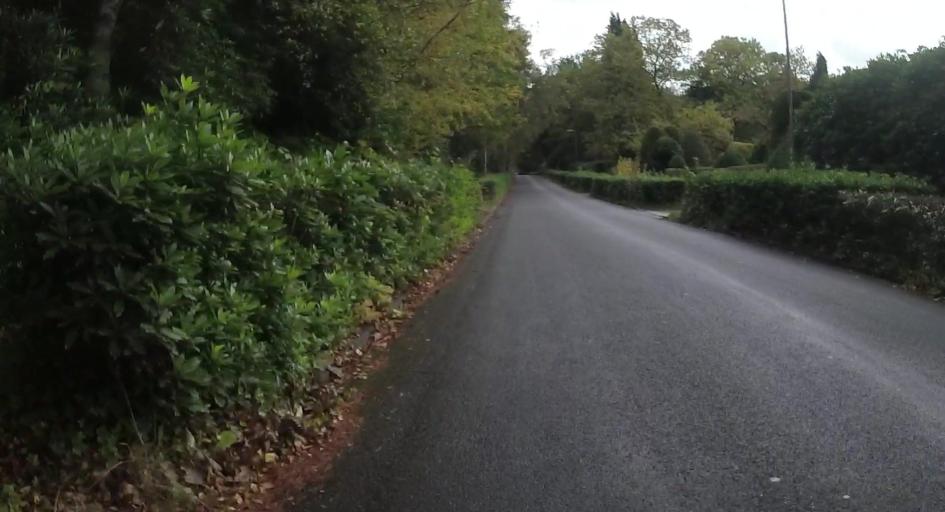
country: GB
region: England
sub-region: Hampshire
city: Fleet
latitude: 51.2811
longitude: -0.8555
